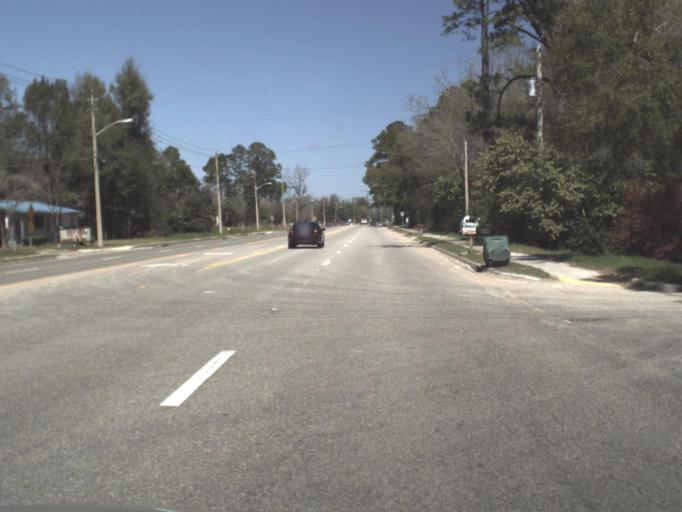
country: US
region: Florida
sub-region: Gadsden County
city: Quincy
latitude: 30.5705
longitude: -84.5931
